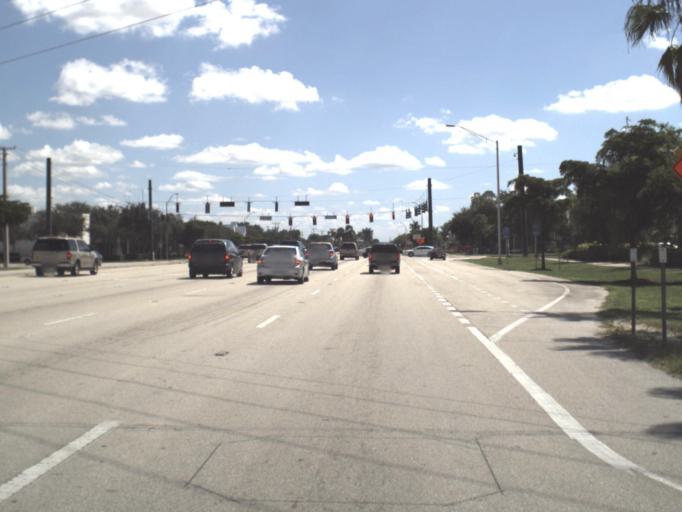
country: US
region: Florida
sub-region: Collier County
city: Lely
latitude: 26.1094
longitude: -81.7501
